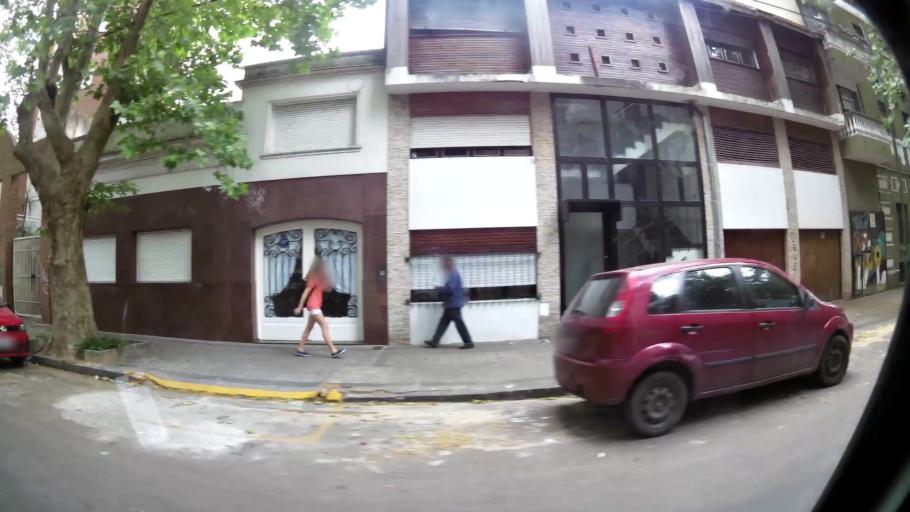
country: AR
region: Buenos Aires
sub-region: Partido de La Plata
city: La Plata
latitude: -34.9141
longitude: -57.9399
